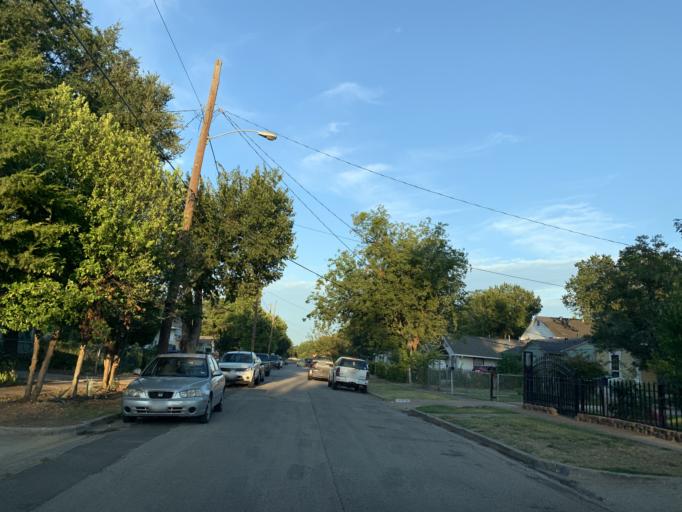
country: US
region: Texas
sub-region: Dallas County
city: Dallas
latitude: 32.7392
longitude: -96.8278
